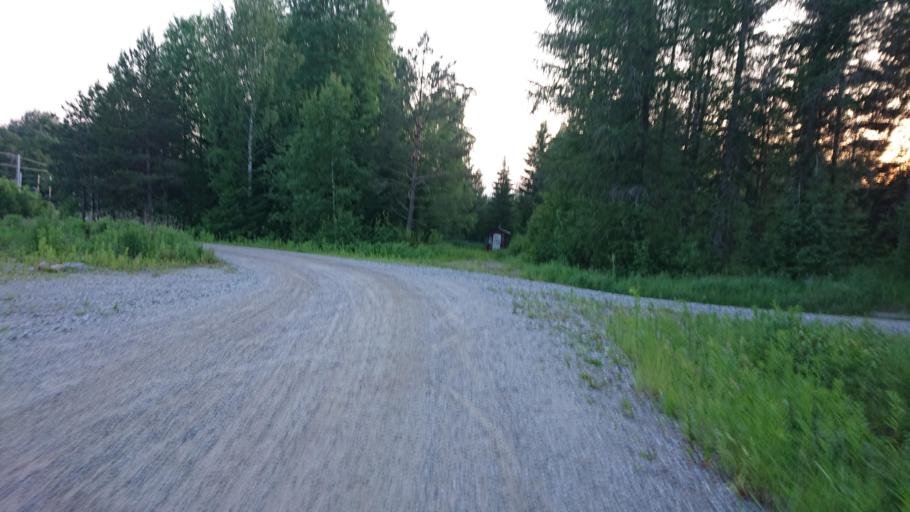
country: SE
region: Stockholm
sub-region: Osterakers Kommun
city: Akersberga
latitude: 59.4658
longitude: 18.1882
